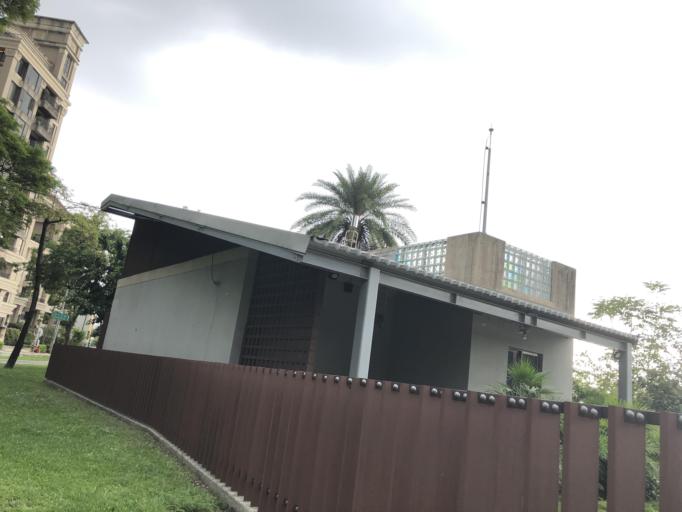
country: TW
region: Kaohsiung
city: Kaohsiung
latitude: 22.6880
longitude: 120.3007
